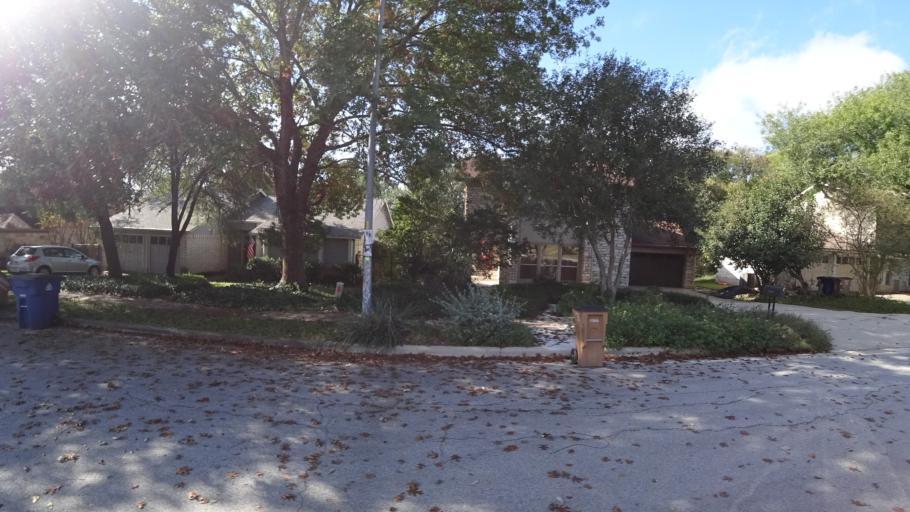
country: US
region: Texas
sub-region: Travis County
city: Shady Hollow
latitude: 30.1947
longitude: -97.8193
